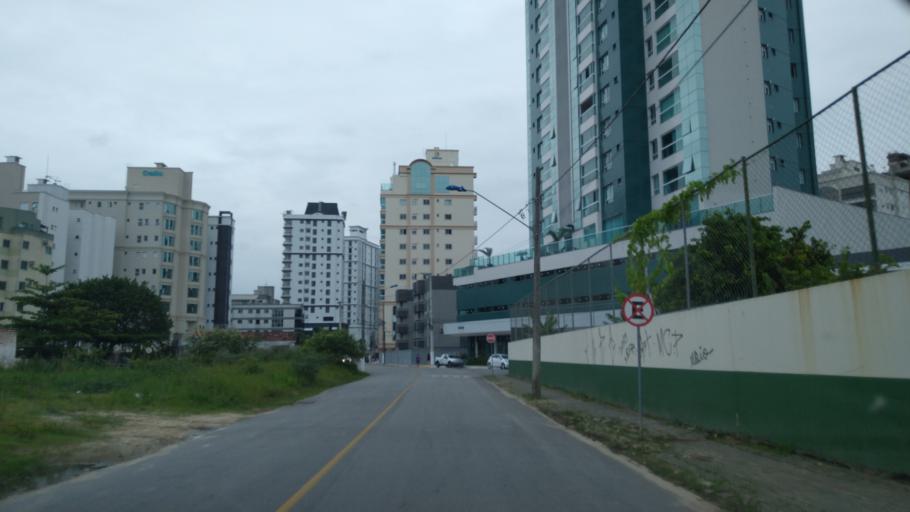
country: BR
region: Santa Catarina
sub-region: Itapema
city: Itapema
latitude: -27.0920
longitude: -48.6114
